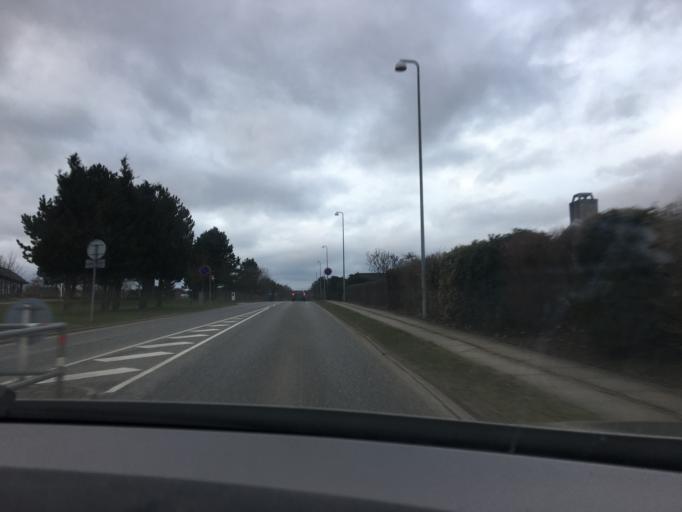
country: DK
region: South Denmark
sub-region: Vejle Kommune
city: Vejle
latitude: 55.7183
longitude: 9.5944
